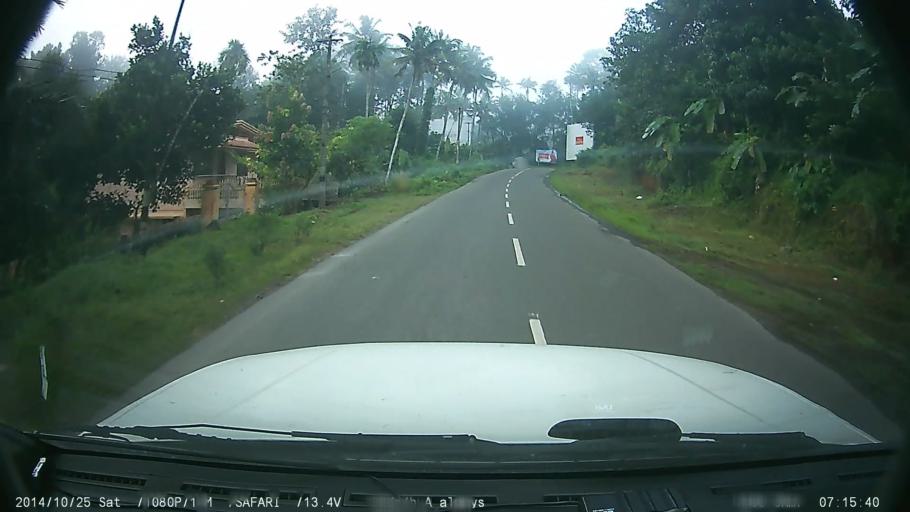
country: IN
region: Kerala
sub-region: Kottayam
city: Palackattumala
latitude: 9.8219
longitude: 76.5856
